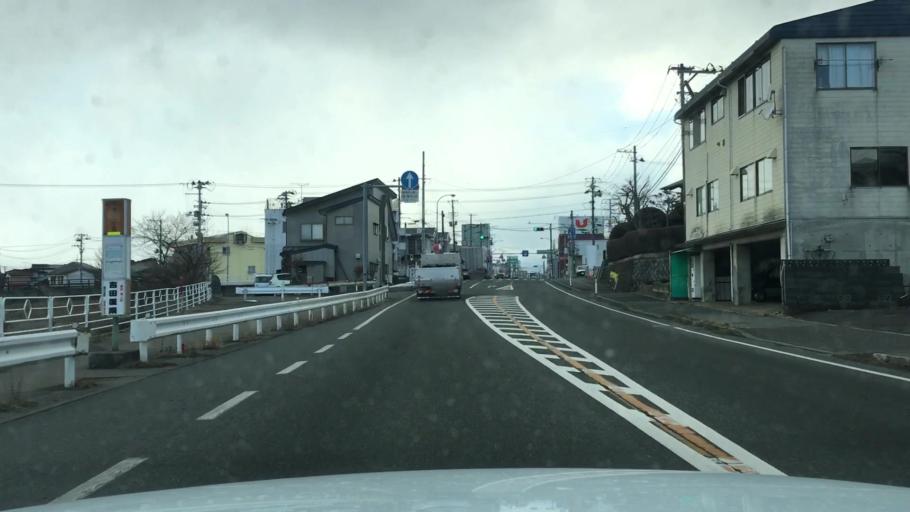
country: JP
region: Iwate
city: Morioka-shi
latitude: 39.6909
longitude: 141.1738
